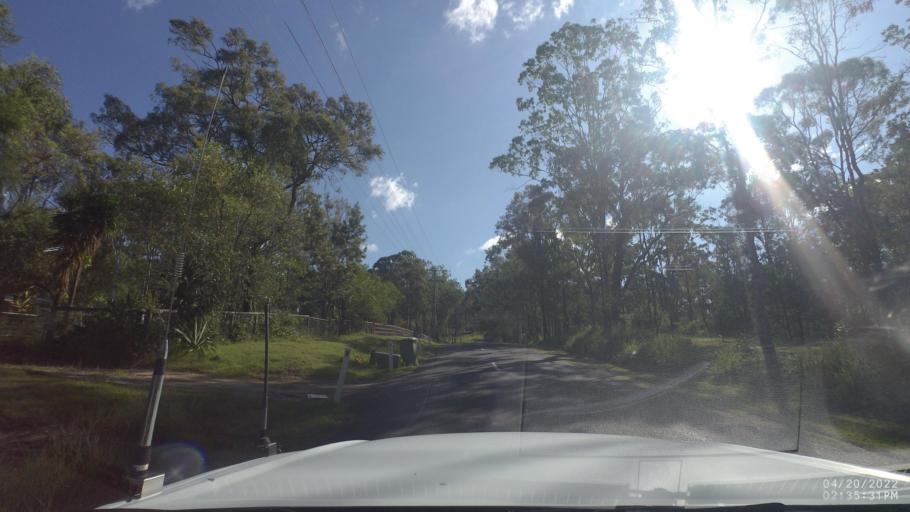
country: AU
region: Queensland
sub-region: Logan
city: Cedar Vale
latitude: -27.8361
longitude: 153.0662
